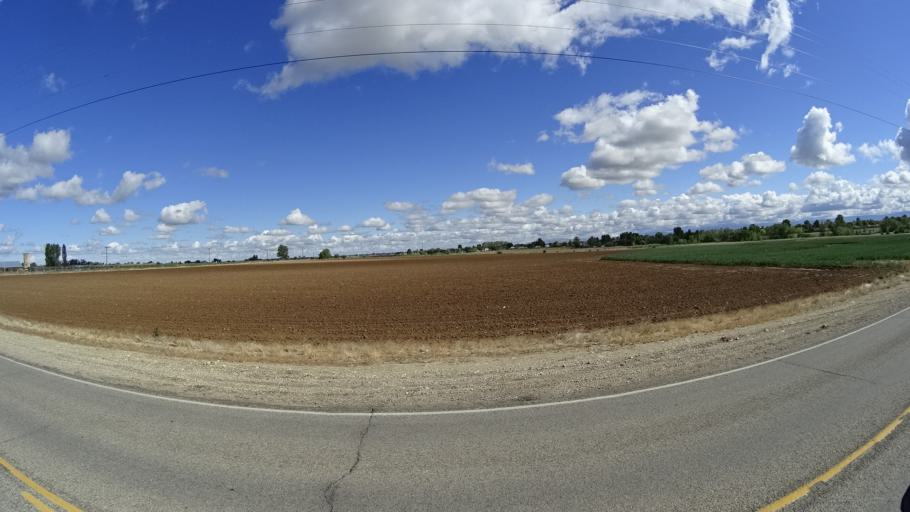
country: US
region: Idaho
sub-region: Ada County
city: Kuna
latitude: 43.4880
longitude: -116.4430
